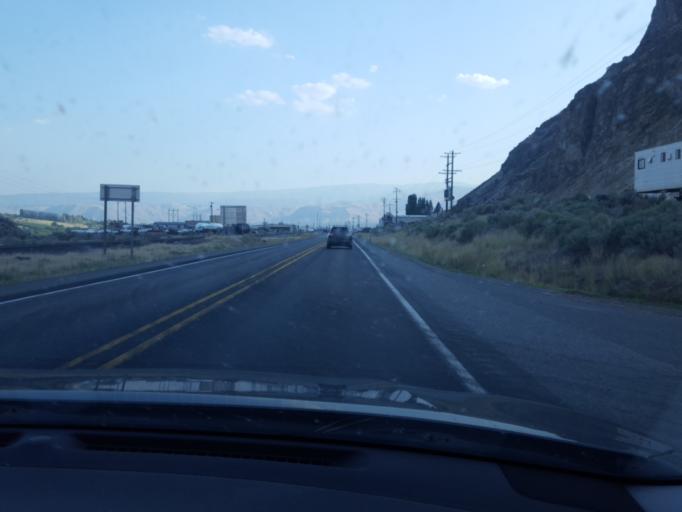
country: US
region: Washington
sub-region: Chelan County
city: Sunnyslope
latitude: 47.4976
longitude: -120.3126
